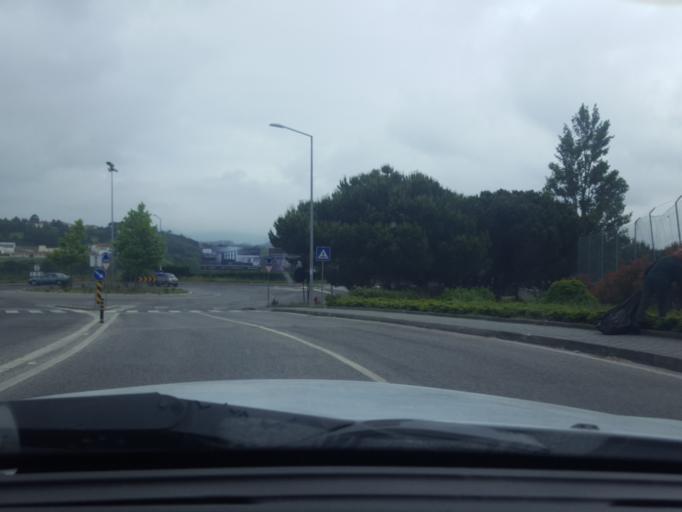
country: PT
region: Leiria
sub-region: Leiria
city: Leiria
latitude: 39.7330
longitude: -8.8228
